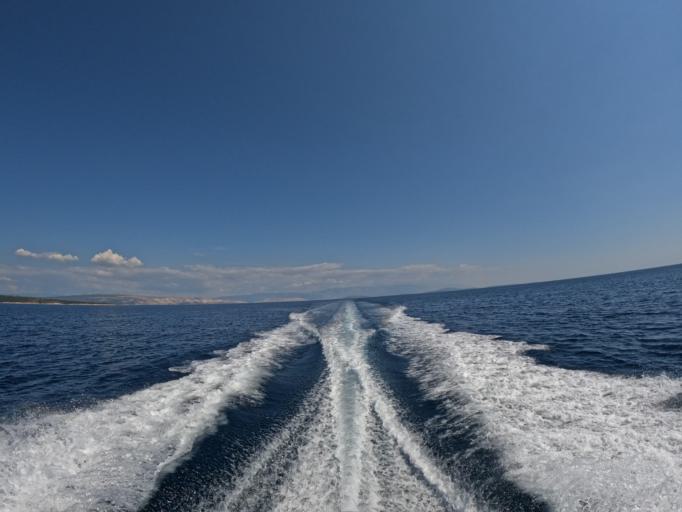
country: HR
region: Primorsko-Goranska
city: Cres
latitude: 44.9399
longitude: 14.4929
